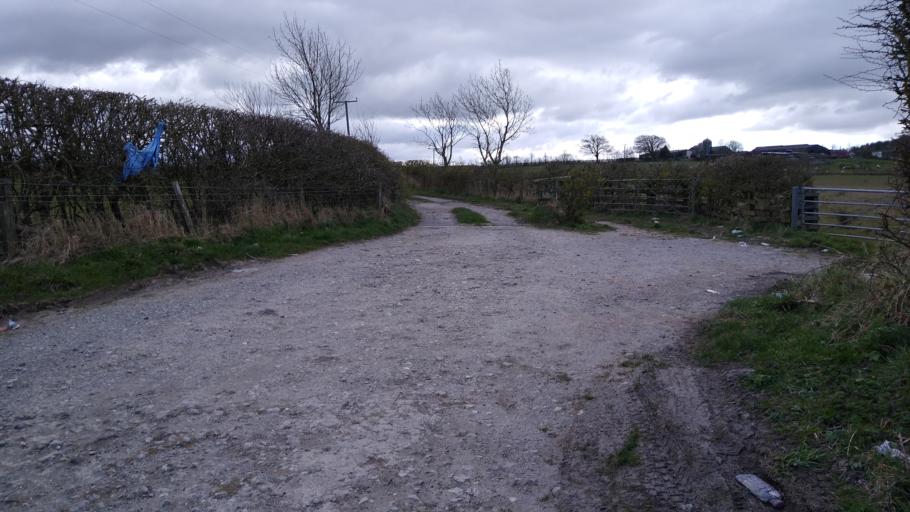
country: GB
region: England
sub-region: Cumbria
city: Dearham
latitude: 54.6909
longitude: -3.4500
